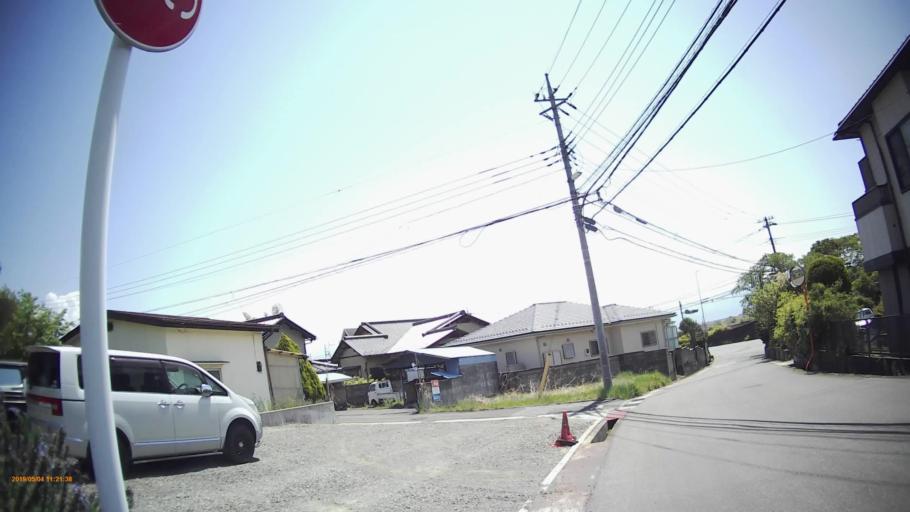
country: JP
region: Yamanashi
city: Nirasaki
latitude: 35.6920
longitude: 138.4749
